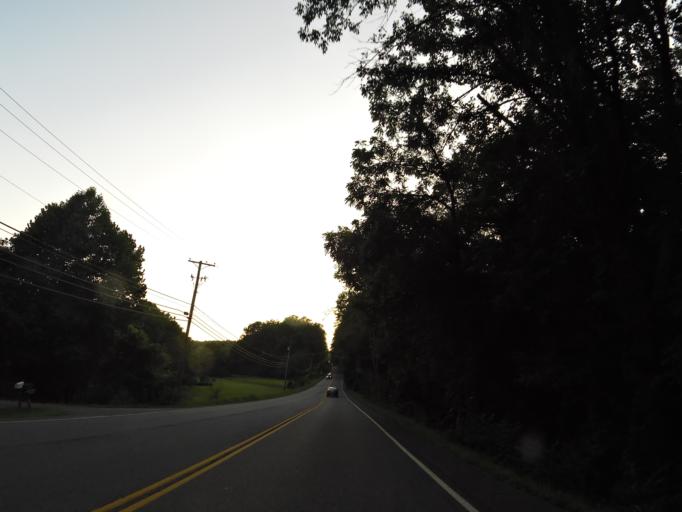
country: US
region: Tennessee
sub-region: Knox County
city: Mascot
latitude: 36.0236
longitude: -83.7096
